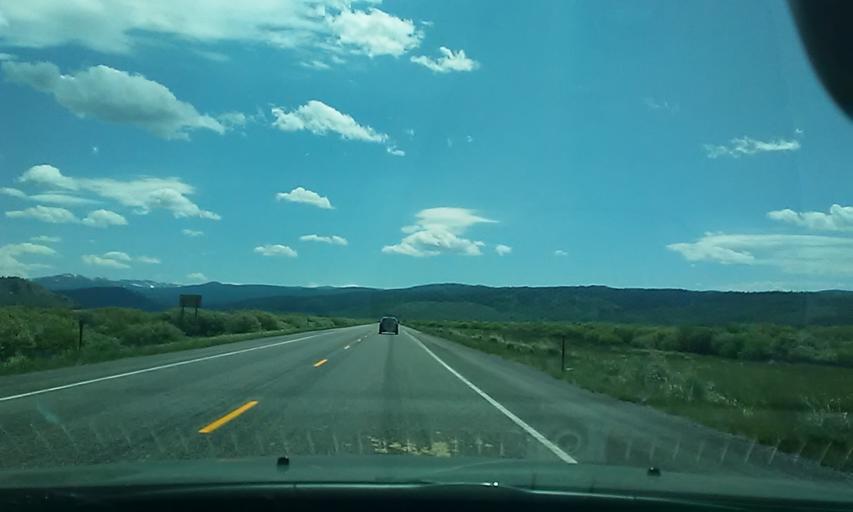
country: US
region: Wyoming
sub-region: Teton County
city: Jackson
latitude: 43.8373
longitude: -110.4362
